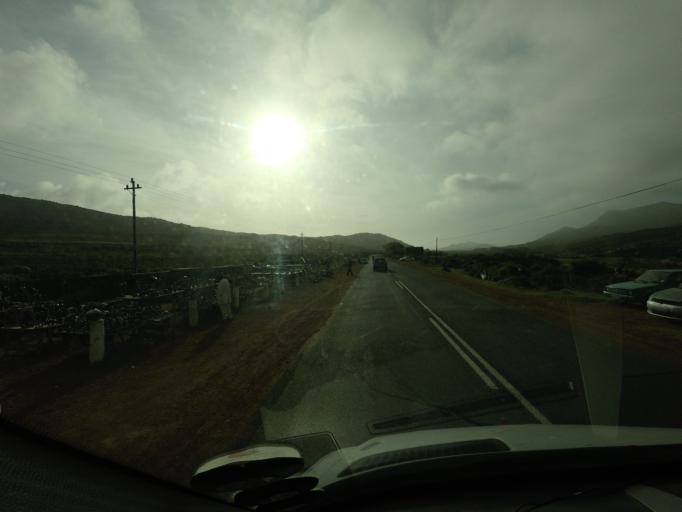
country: ZA
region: Western Cape
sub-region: City of Cape Town
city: Retreat
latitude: -34.2574
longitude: 18.4555
